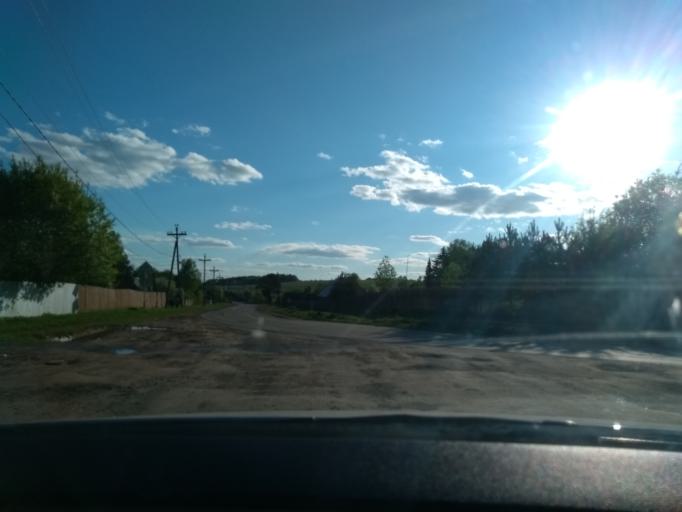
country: RU
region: Perm
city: Sylva
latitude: 57.8370
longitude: 56.6775
